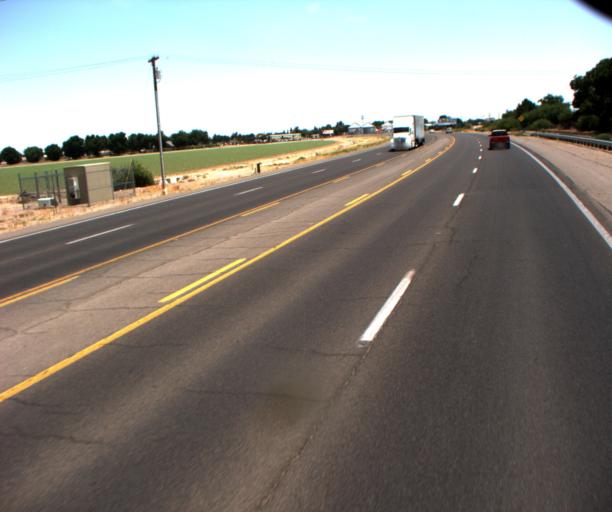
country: US
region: Arizona
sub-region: Graham County
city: Thatcher
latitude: 32.8515
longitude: -109.7763
